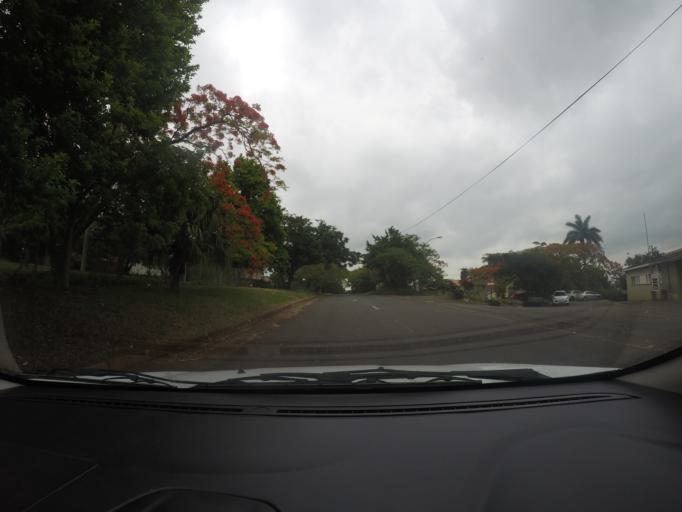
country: ZA
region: KwaZulu-Natal
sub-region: uThungulu District Municipality
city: Empangeni
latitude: -28.7467
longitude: 31.8958
